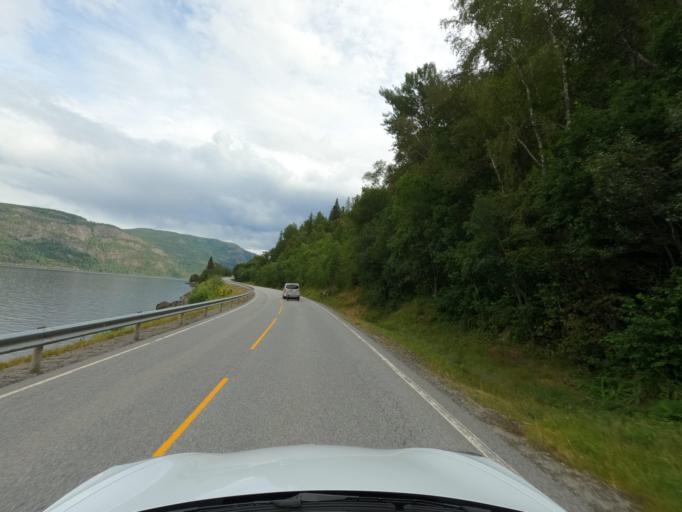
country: NO
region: Telemark
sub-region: Tinn
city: Rjukan
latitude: 59.9203
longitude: 8.8626
